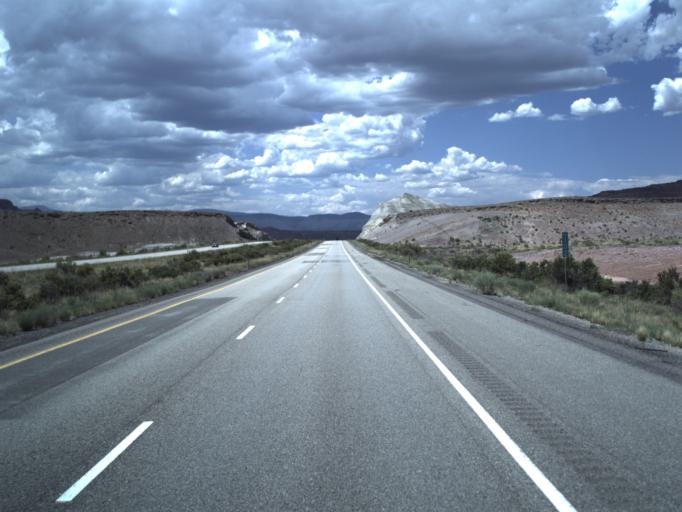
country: US
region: Utah
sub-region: Emery County
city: Ferron
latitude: 38.8181
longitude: -111.1645
